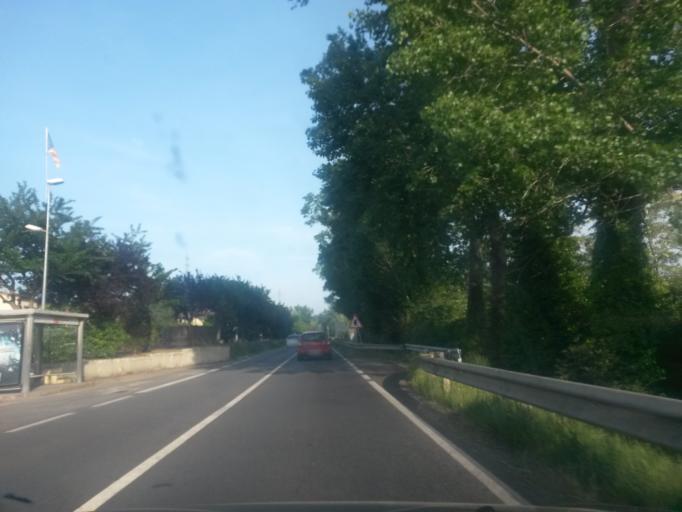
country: ES
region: Catalonia
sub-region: Provincia de Girona
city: Vilablareix
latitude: 41.9697
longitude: 2.7643
